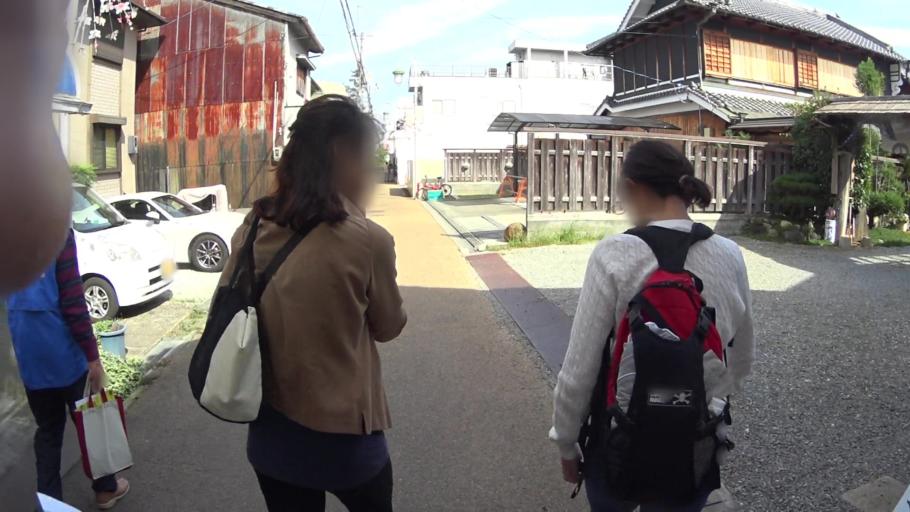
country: JP
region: Nara
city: Sakurai
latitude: 34.5274
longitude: 135.8475
